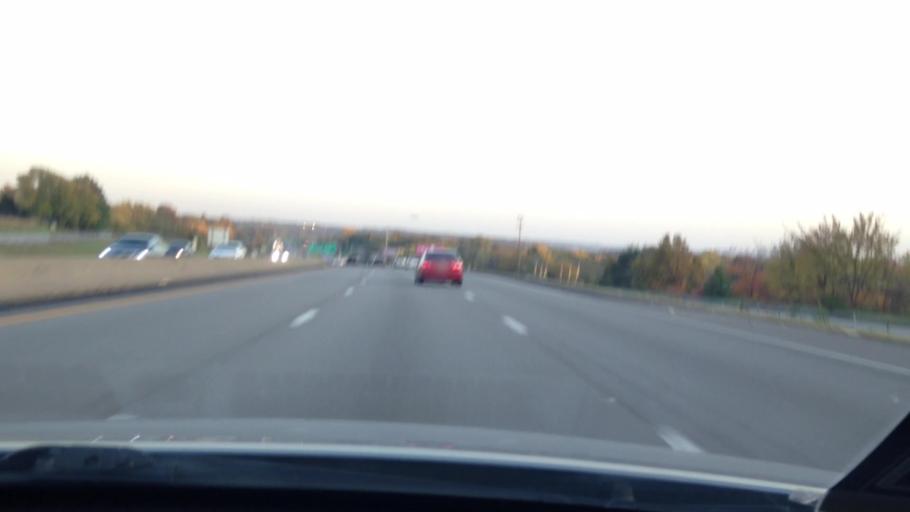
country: US
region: Missouri
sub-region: Platte County
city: Riverside
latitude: 39.2057
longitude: -94.6344
